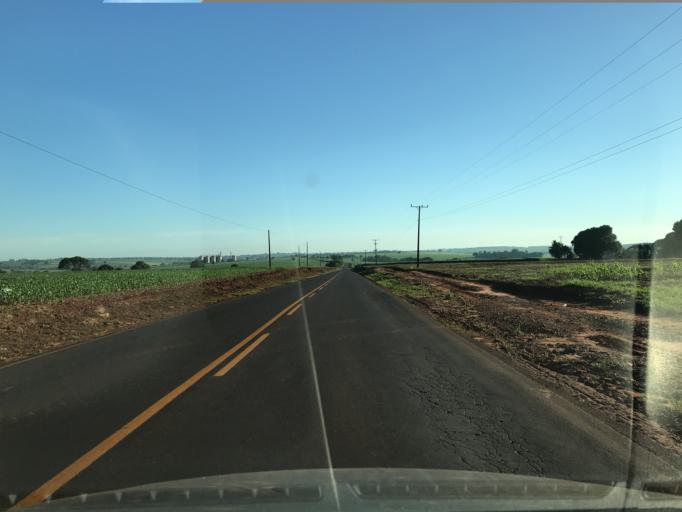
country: BR
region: Parana
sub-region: Palotina
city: Palotina
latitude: -24.1340
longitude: -53.8549
